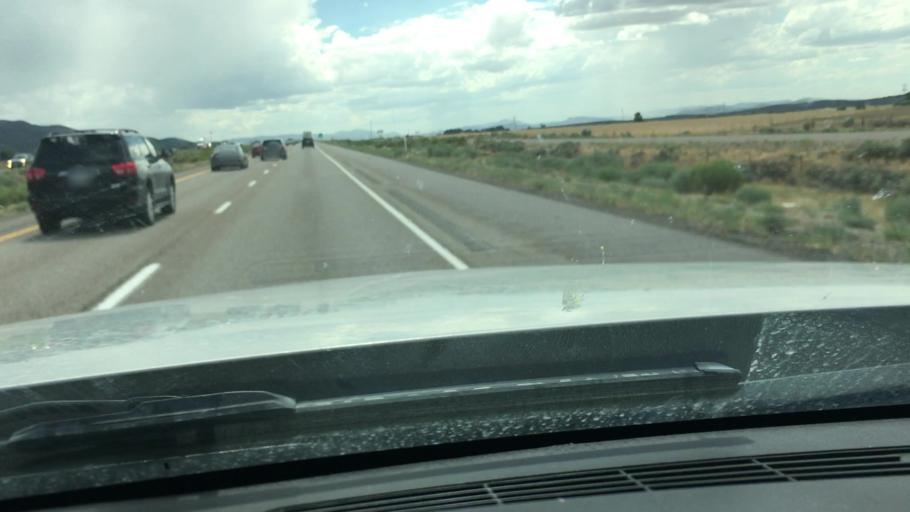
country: US
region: Utah
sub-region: Iron County
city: Enoch
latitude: 37.8130
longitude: -112.9297
